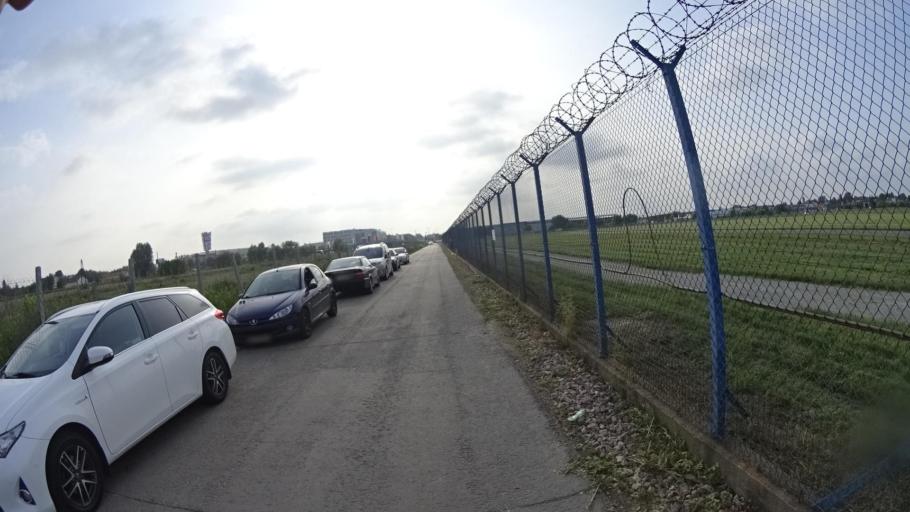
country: PL
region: Masovian Voivodeship
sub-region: Warszawa
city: Wlochy
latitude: 52.1708
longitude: 20.9429
